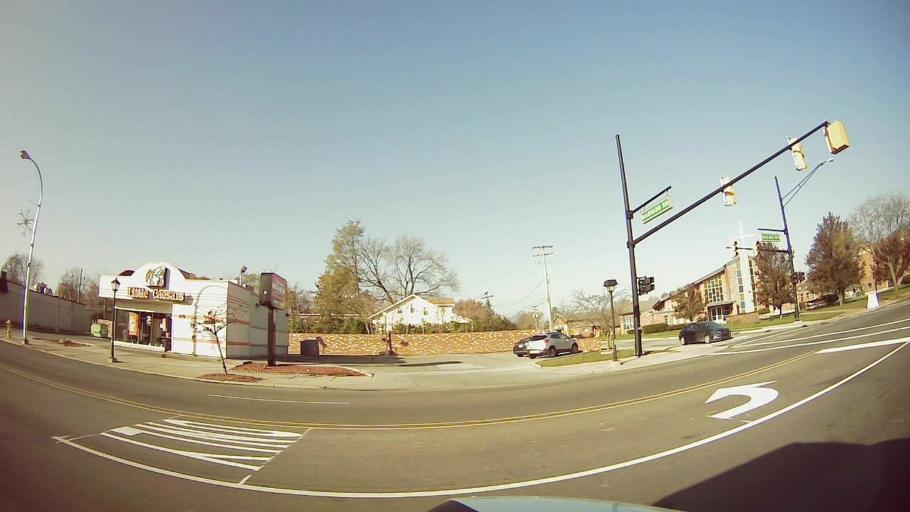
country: US
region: Michigan
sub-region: Oakland County
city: Berkley
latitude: 42.4917
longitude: -83.1834
